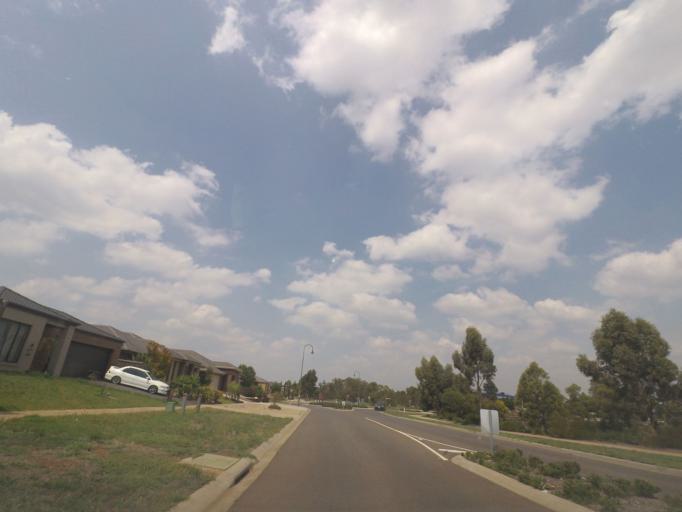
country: AU
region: Victoria
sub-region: Melton
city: Melton West
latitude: -37.6666
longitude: 144.5488
